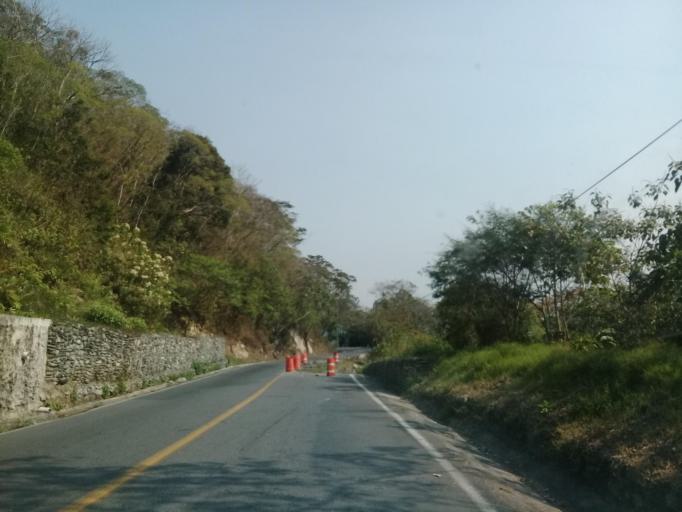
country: MX
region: Veracruz
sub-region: Ixtaczoquitlan
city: Campo Chico
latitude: 18.8431
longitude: -97.0276
